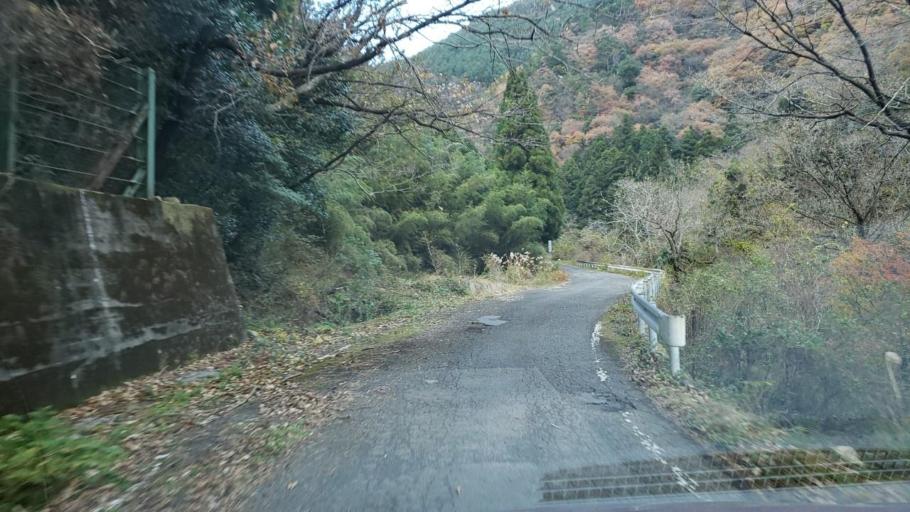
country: JP
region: Tokushima
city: Wakimachi
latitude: 34.1393
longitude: 134.2302
